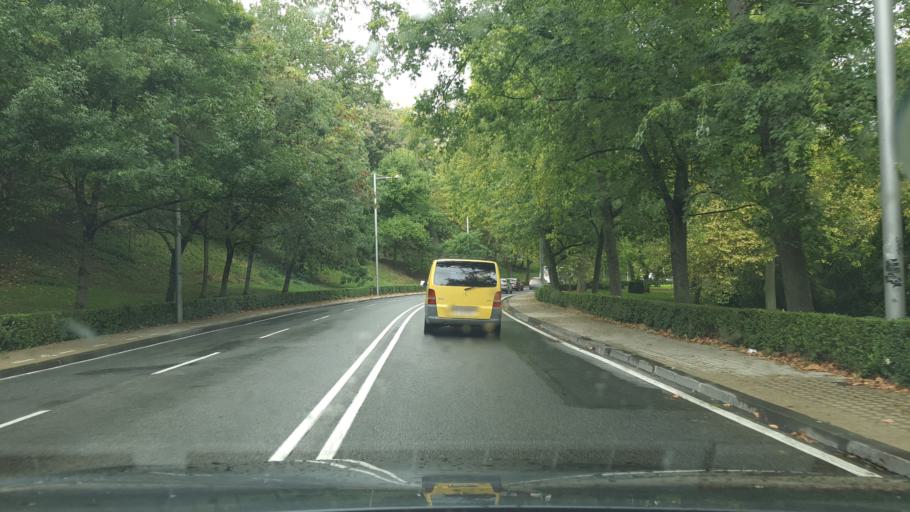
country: ES
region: Navarre
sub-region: Provincia de Navarra
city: Pamplona
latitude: 42.8184
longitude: -1.6383
